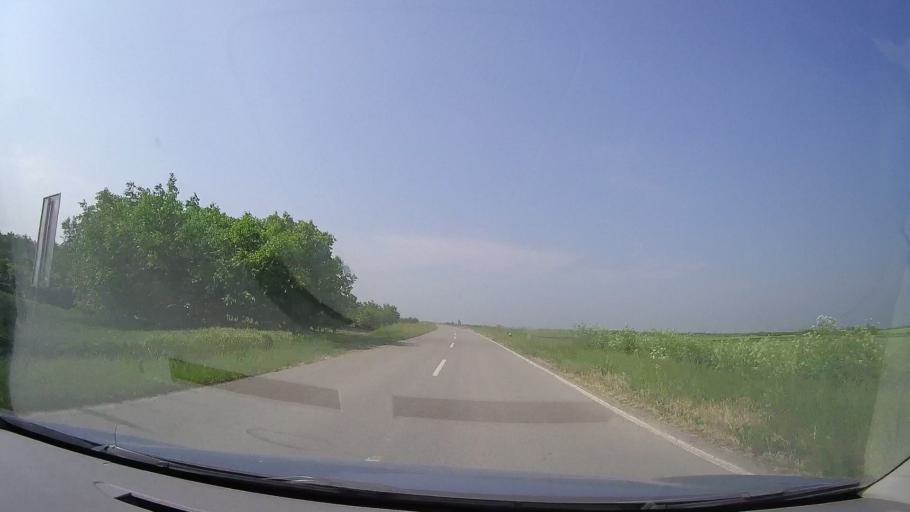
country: RS
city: Jasa Tomic
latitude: 45.4311
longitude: 20.8405
